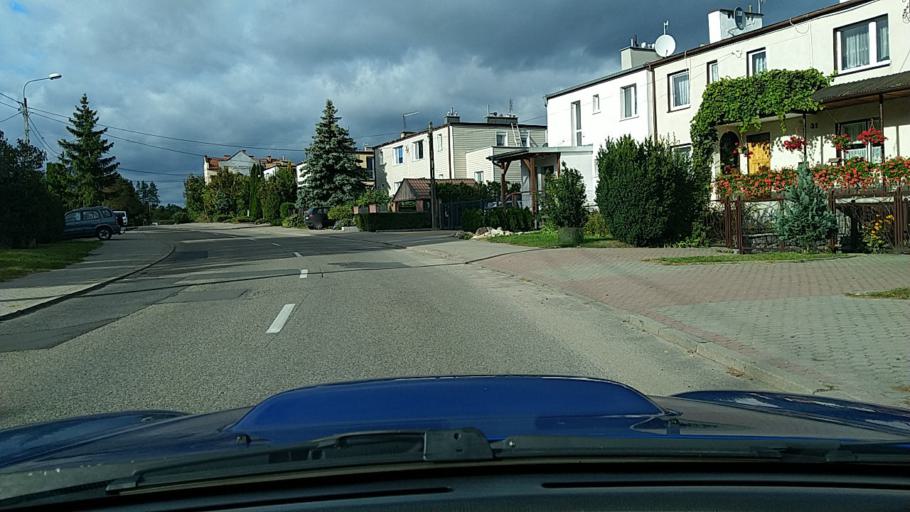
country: PL
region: Warmian-Masurian Voivodeship
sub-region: Olsztyn
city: Kortowo
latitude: 53.7674
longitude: 20.4357
